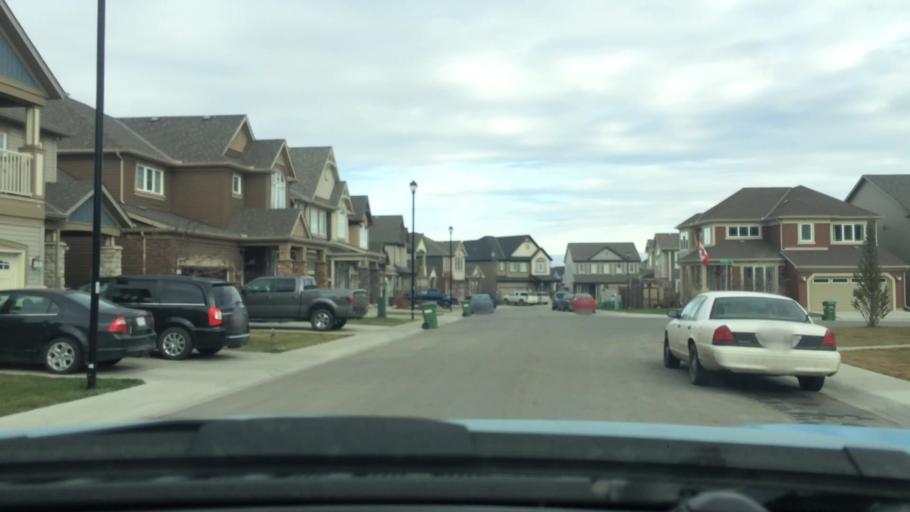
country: CA
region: Alberta
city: Airdrie
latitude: 51.2602
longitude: -114.0349
